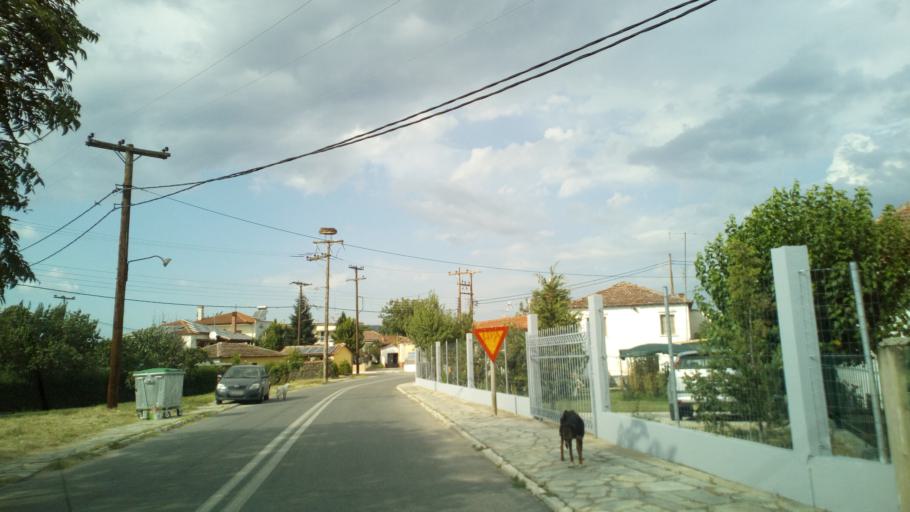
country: GR
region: Central Macedonia
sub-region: Nomos Thessalonikis
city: Gerakarou
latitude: 40.5721
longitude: 23.2865
